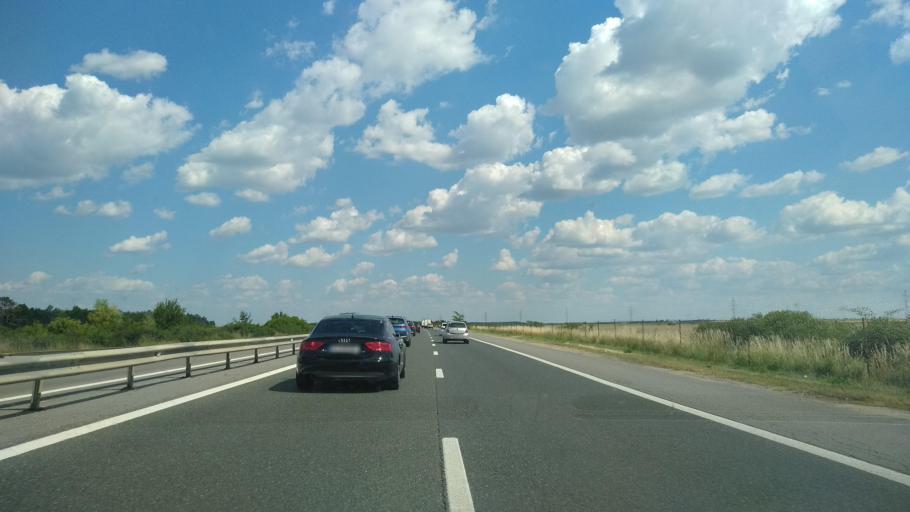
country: RO
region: Arges
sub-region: Comuna Ratesti
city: Patuleni
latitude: 44.7154
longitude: 25.1618
